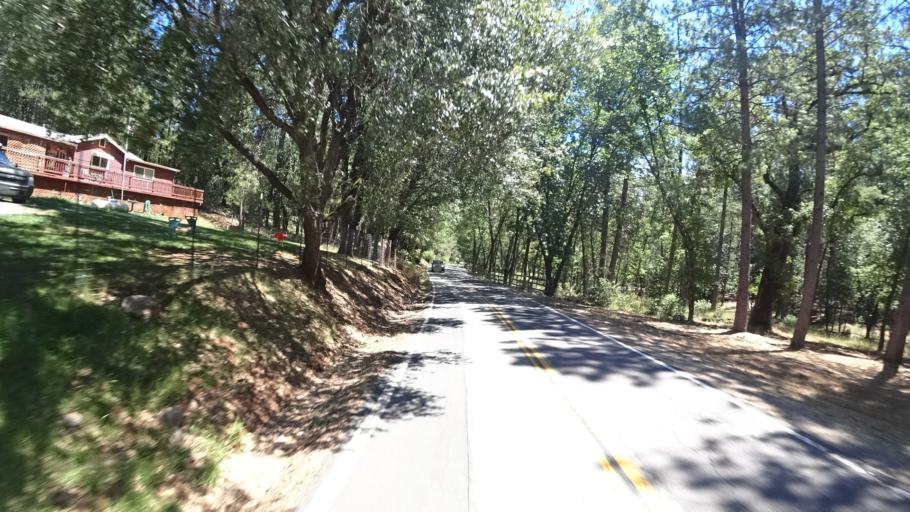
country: US
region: California
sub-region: Amador County
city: Pioneer
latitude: 38.3457
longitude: -120.5698
